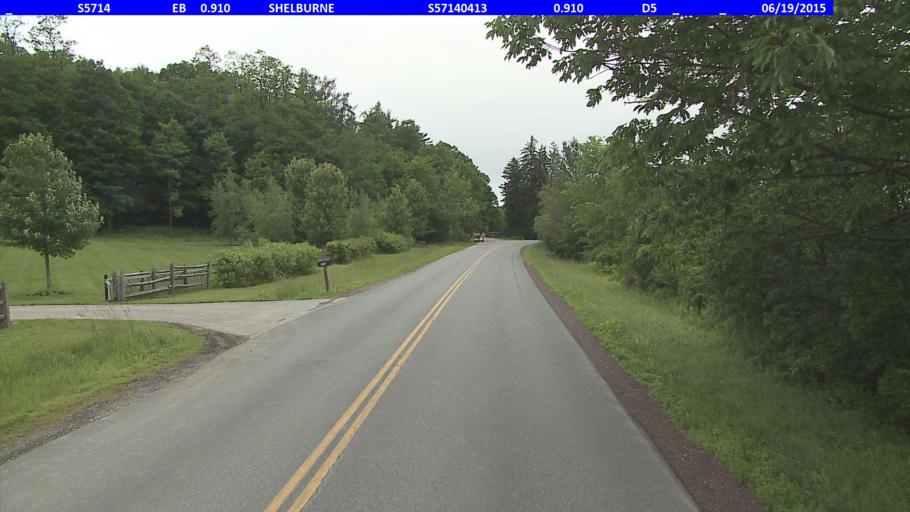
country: US
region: Vermont
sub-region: Chittenden County
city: Burlington
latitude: 44.3853
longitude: -73.2437
